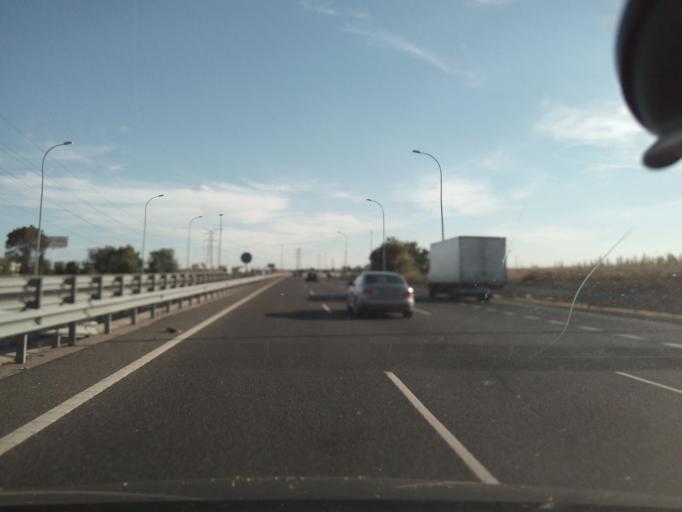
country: ES
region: Madrid
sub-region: Provincia de Madrid
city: Pinto
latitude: 40.2855
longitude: -3.6805
